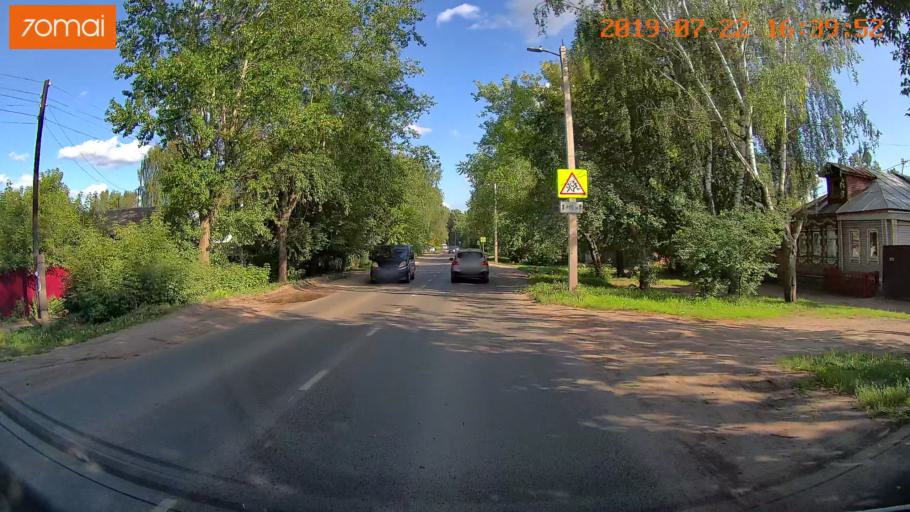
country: RU
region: Ivanovo
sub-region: Gorod Ivanovo
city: Ivanovo
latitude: 57.0253
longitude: 40.9538
